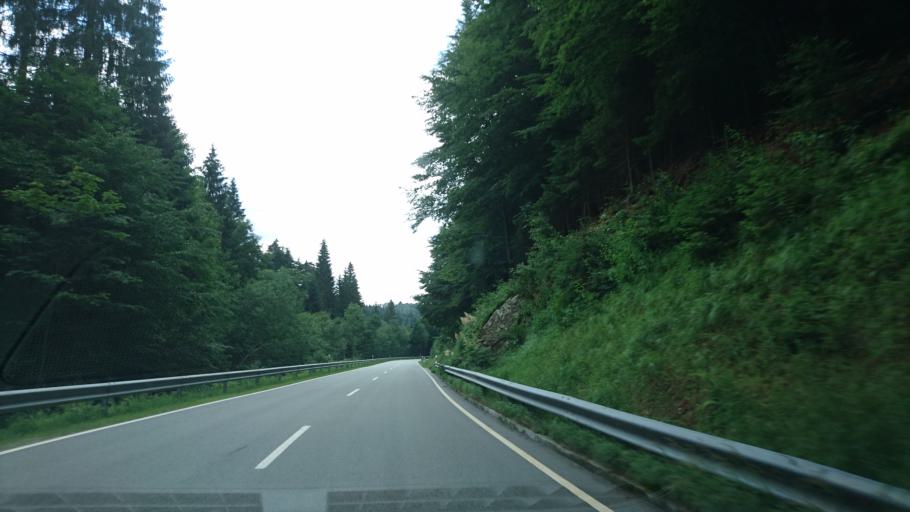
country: DE
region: Bavaria
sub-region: Lower Bavaria
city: Mauth
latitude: 48.8794
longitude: 13.5750
